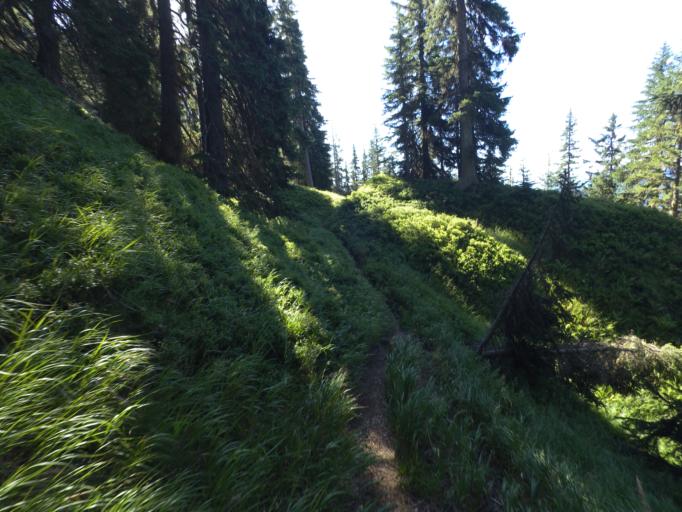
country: AT
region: Salzburg
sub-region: Politischer Bezirk Sankt Johann im Pongau
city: Goldegg
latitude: 47.3624
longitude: 13.0672
